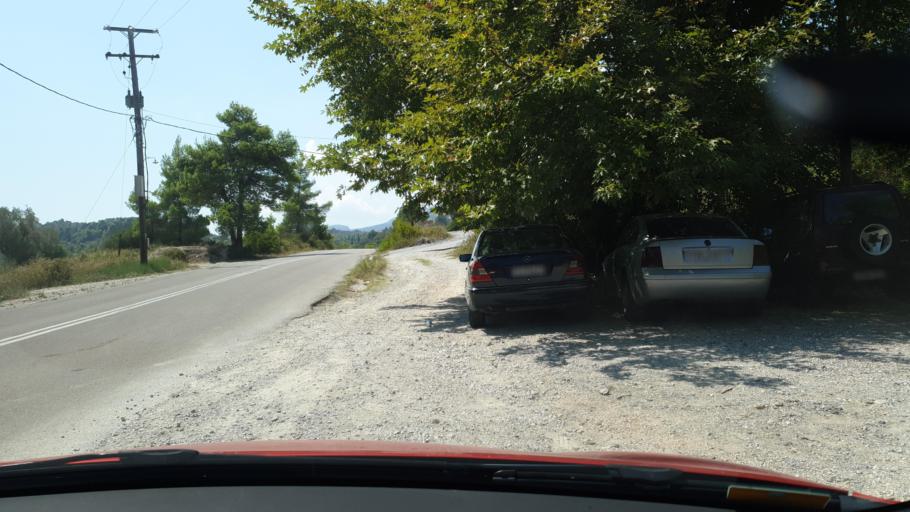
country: GR
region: Central Greece
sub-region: Nomos Evvoias
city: Oxilithos
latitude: 38.5947
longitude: 24.0746
